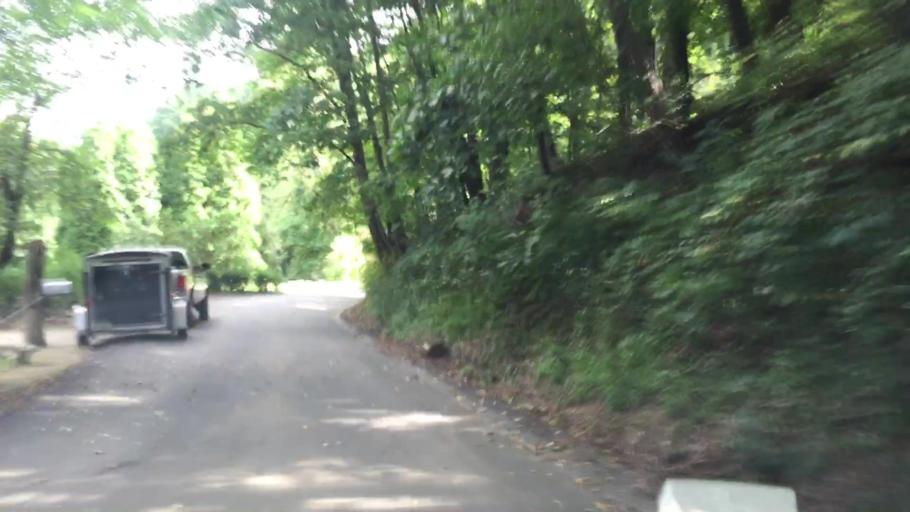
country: US
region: Pennsylvania
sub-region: Allegheny County
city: Millvale
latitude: 40.5024
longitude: -80.0005
